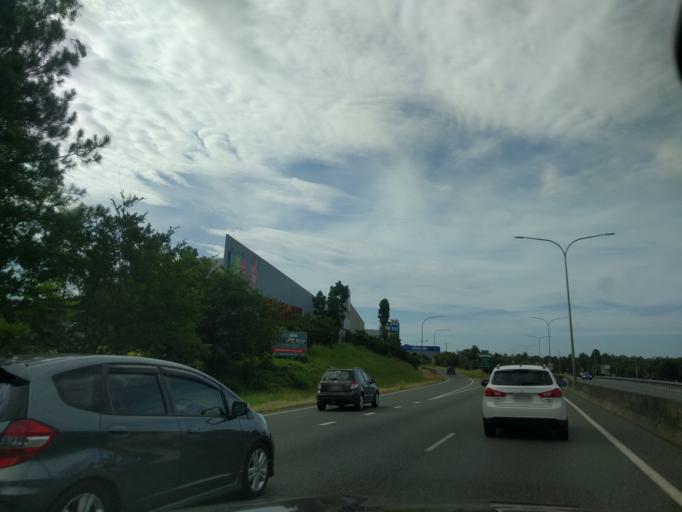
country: AU
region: Queensland
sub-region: Brisbane
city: Seventeen Mile Rocks
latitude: -27.5297
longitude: 152.9467
